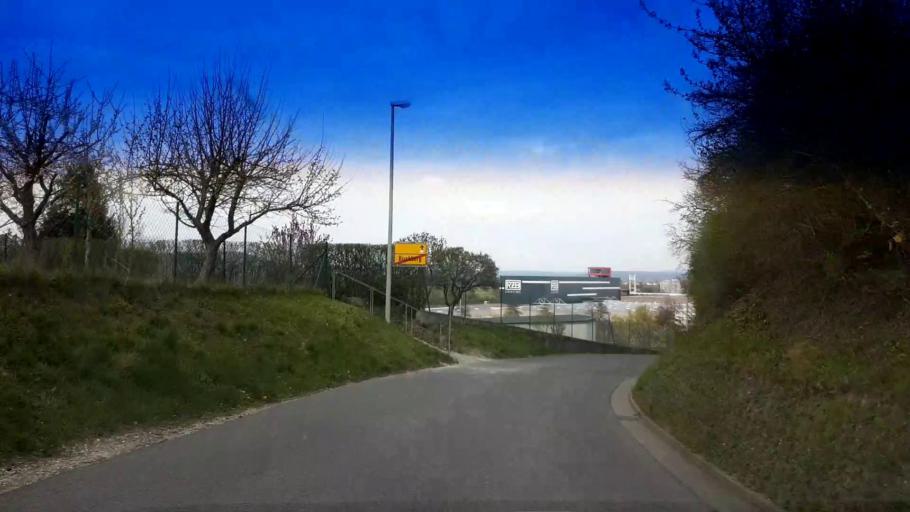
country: DE
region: Bavaria
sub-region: Upper Franconia
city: Bischberg
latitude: 49.9065
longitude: 10.8448
